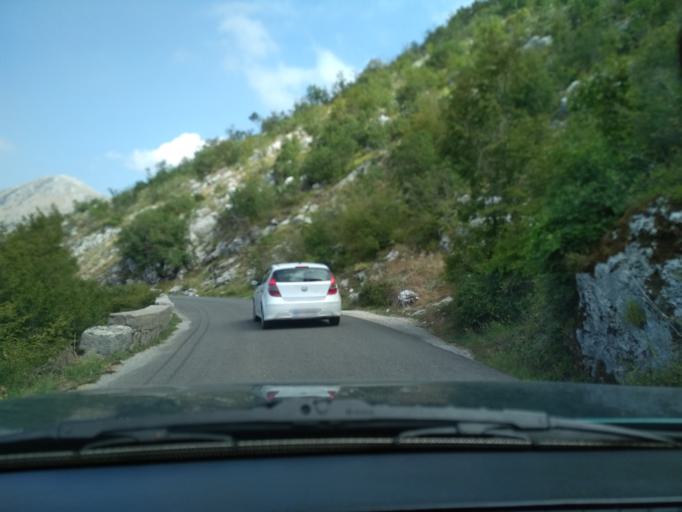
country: ME
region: Kotor
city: Kotor
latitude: 42.4121
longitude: 18.7904
